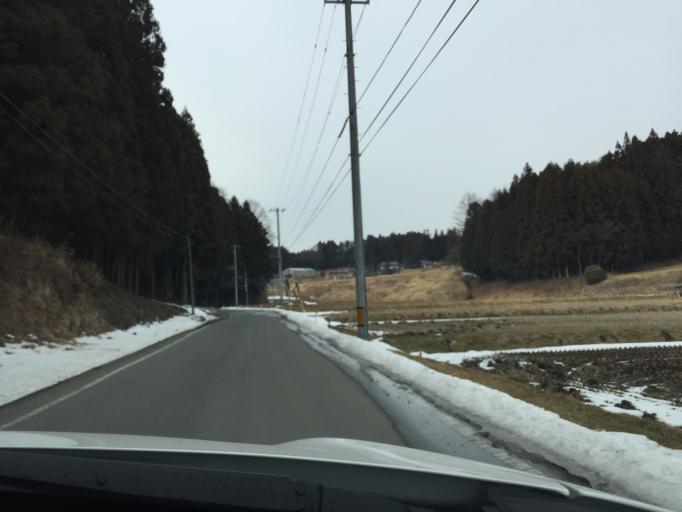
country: JP
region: Fukushima
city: Ishikawa
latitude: 37.1961
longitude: 140.5732
